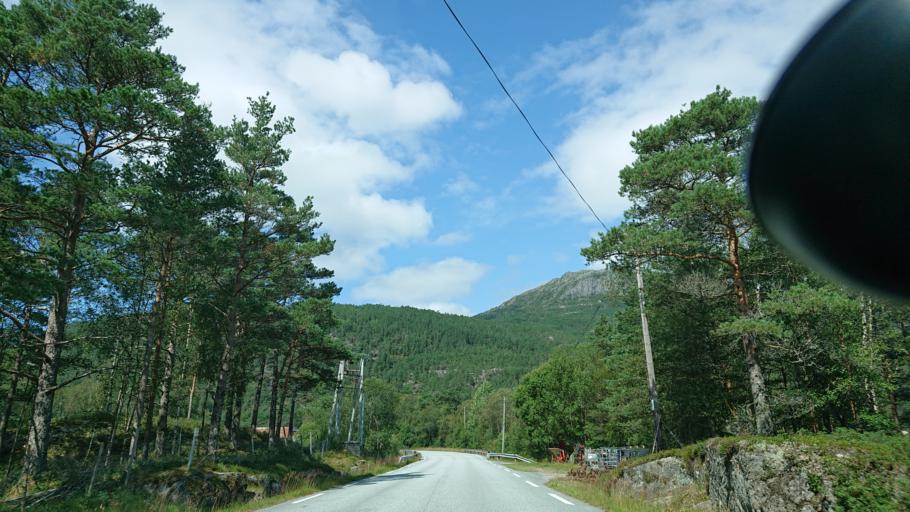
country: NO
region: Rogaland
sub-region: Hjelmeland
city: Hjelmelandsvagen
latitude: 59.2369
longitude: 6.2605
